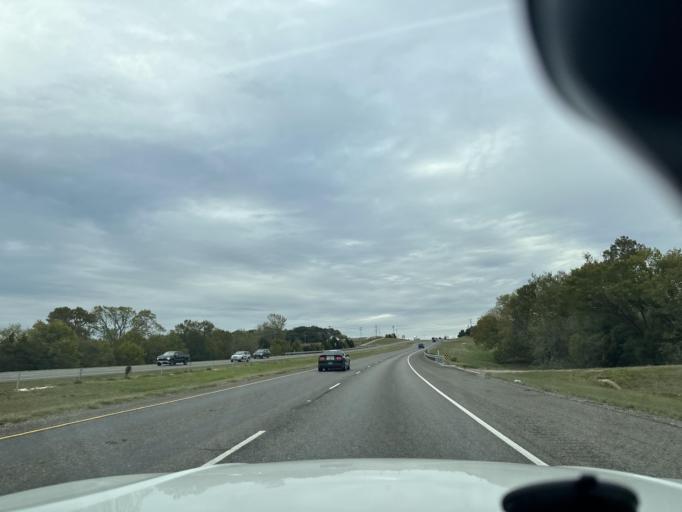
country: US
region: Texas
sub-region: Burleson County
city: Somerville
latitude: 30.1831
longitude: -96.5863
